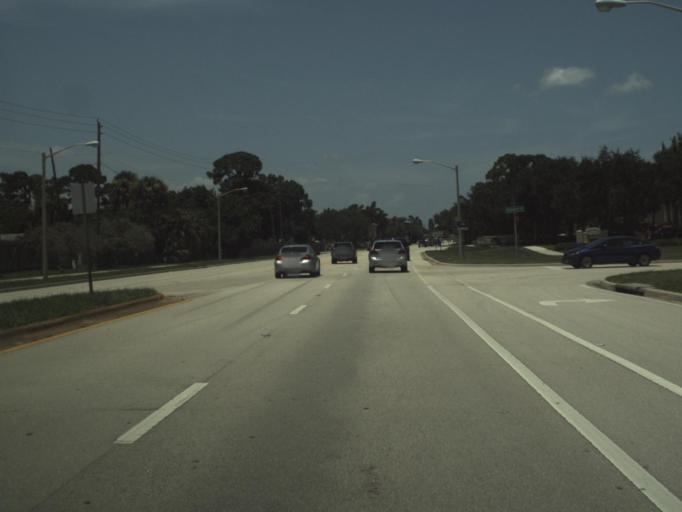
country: US
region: Florida
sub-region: Martin County
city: Sewall's Point
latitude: 27.1913
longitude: -80.2239
